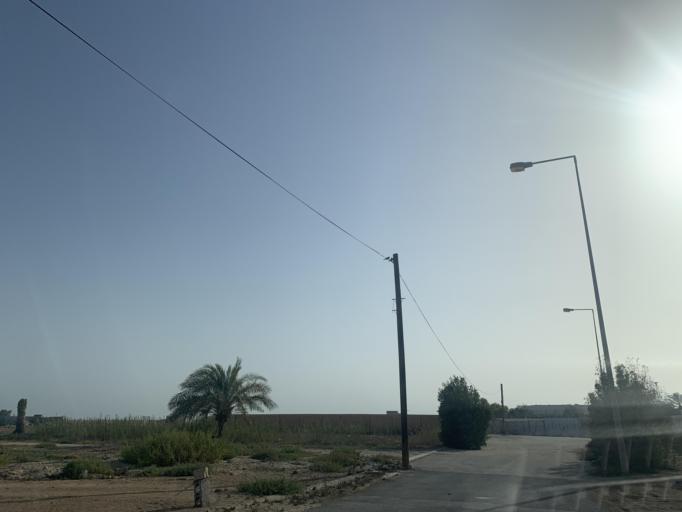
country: BH
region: Central Governorate
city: Madinat Hamad
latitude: 26.1894
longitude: 50.4584
